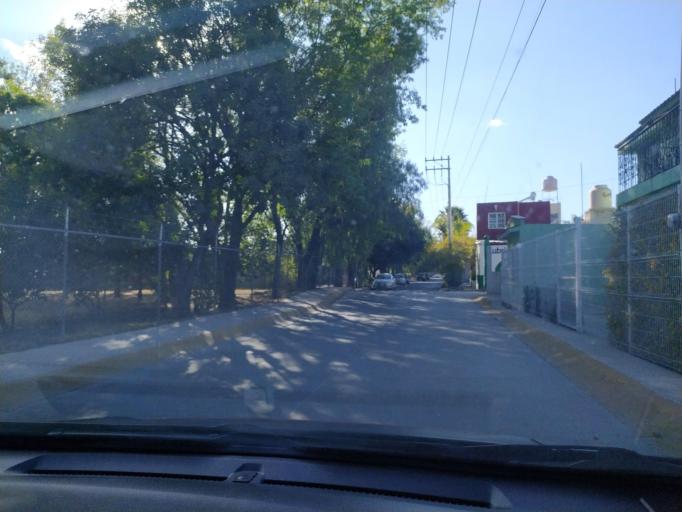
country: LA
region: Oudomxai
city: Muang La
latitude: 21.0270
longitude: 101.8274
